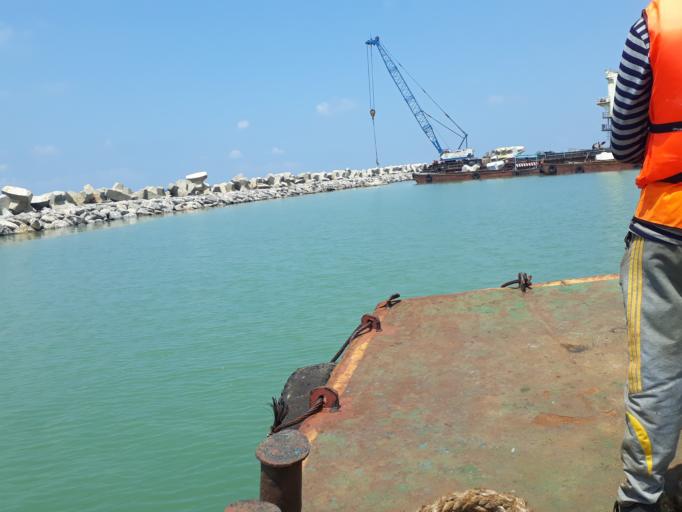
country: LK
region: Western
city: Colombo
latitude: 6.9270
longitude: 79.8228
